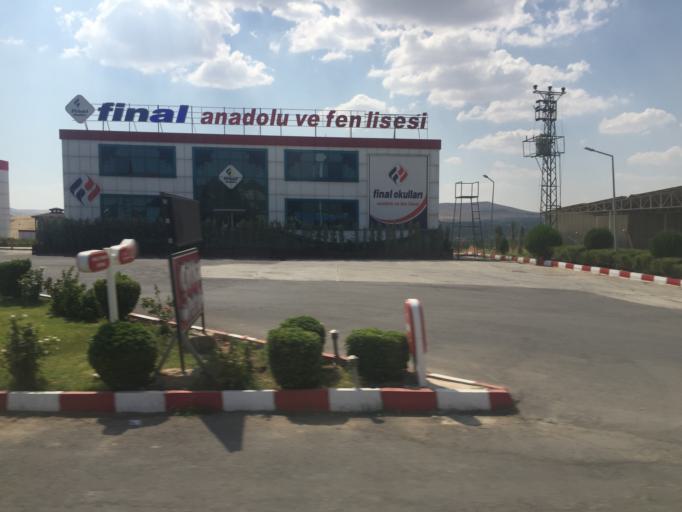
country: TR
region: Sanliurfa
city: Sanliurfa
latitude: 37.2451
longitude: 38.7935
